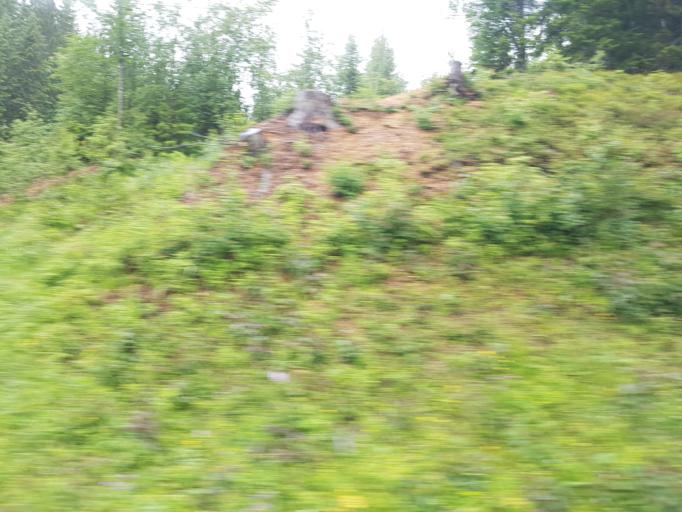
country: NO
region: Sor-Trondelag
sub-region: Selbu
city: Mebonden
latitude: 63.3064
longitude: 11.0787
